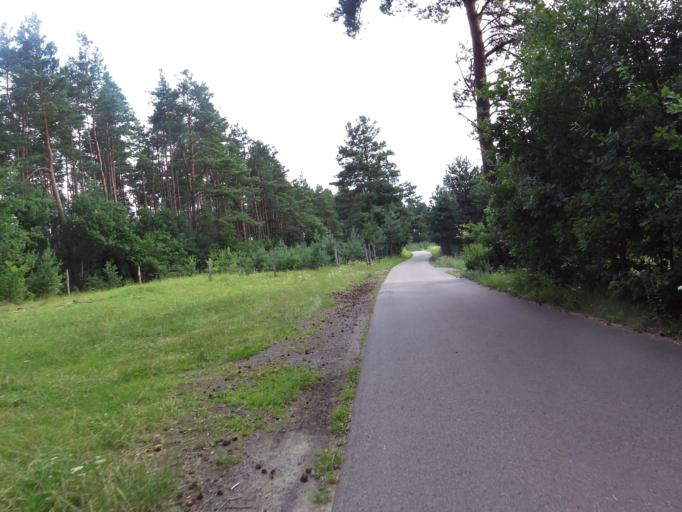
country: DE
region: Brandenburg
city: Lychen
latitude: 53.2276
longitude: 13.2748
